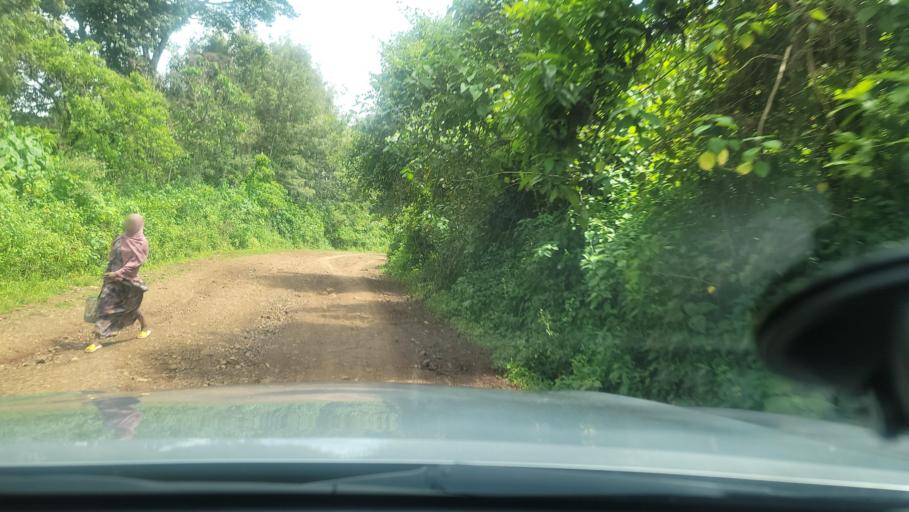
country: ET
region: Oromiya
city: Agaro
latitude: 7.8034
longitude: 36.4164
